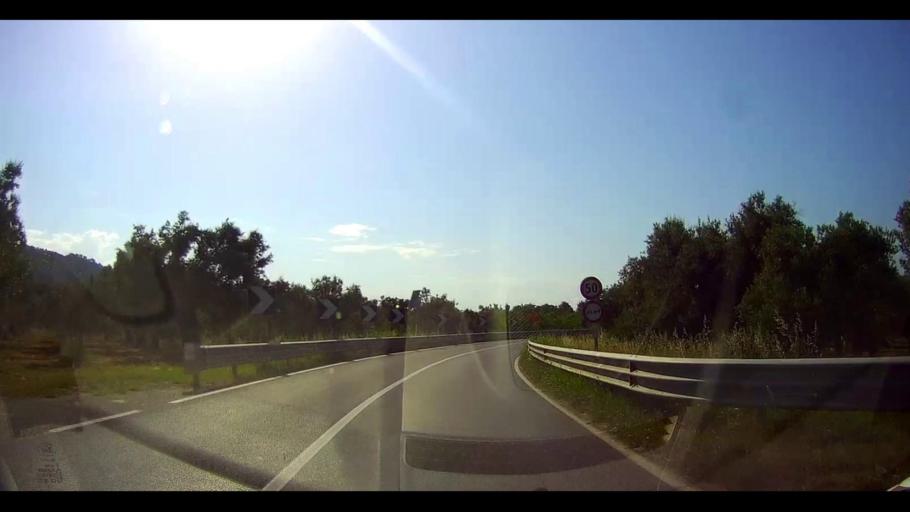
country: IT
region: Calabria
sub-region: Provincia di Cosenza
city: Cariati
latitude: 39.4821
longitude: 16.9782
